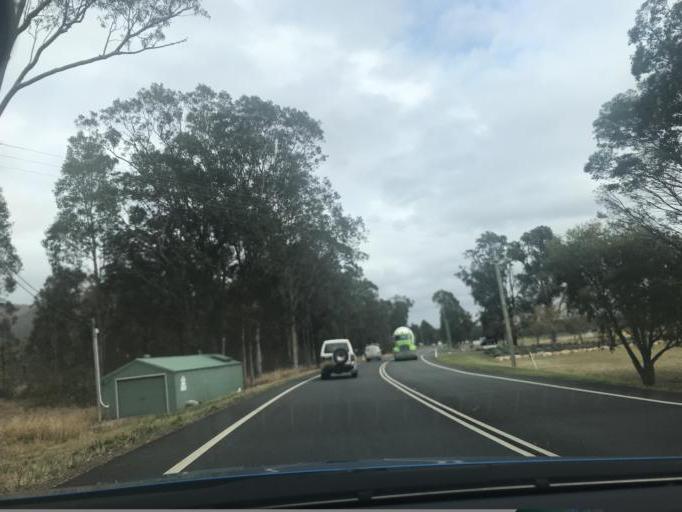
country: AU
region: New South Wales
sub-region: Cessnock
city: Cessnock
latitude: -32.7677
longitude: 151.2641
